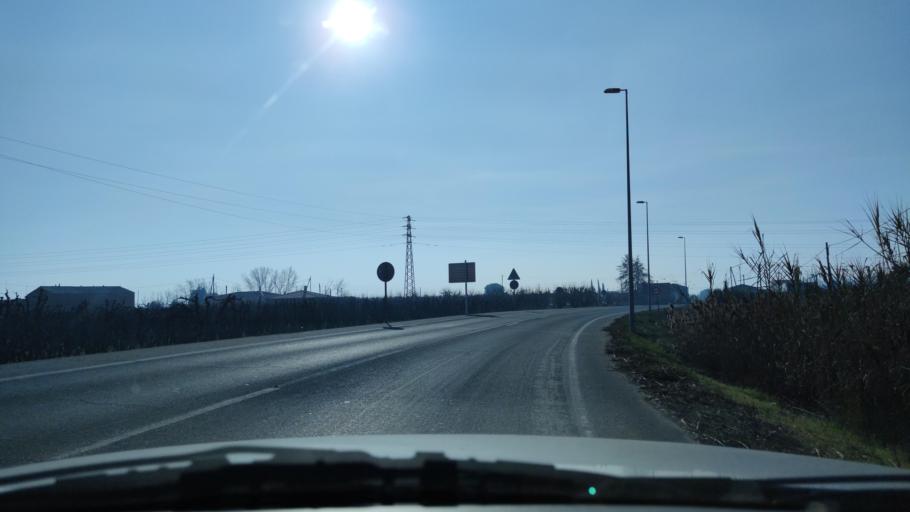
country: ES
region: Catalonia
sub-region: Provincia de Lleida
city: Lleida
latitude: 41.6455
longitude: 0.6355
